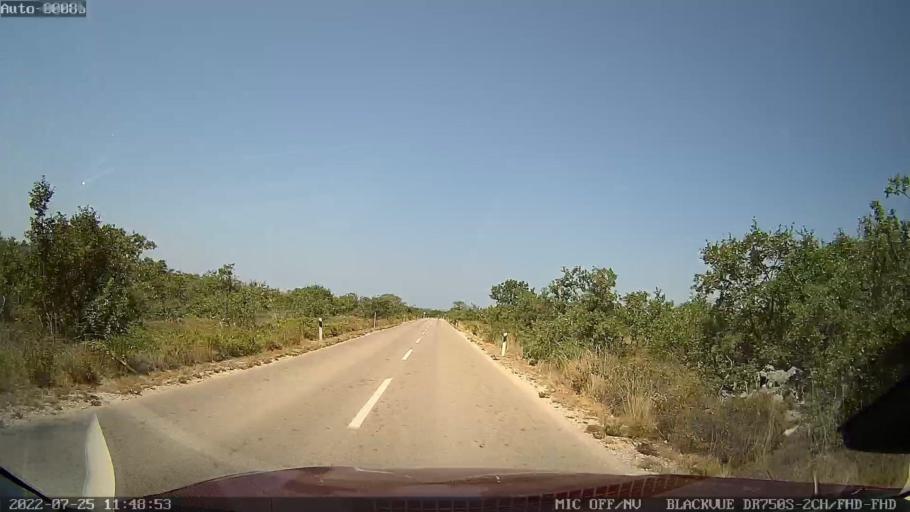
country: HR
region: Zadarska
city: Vrsi
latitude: 44.2347
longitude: 15.2916
